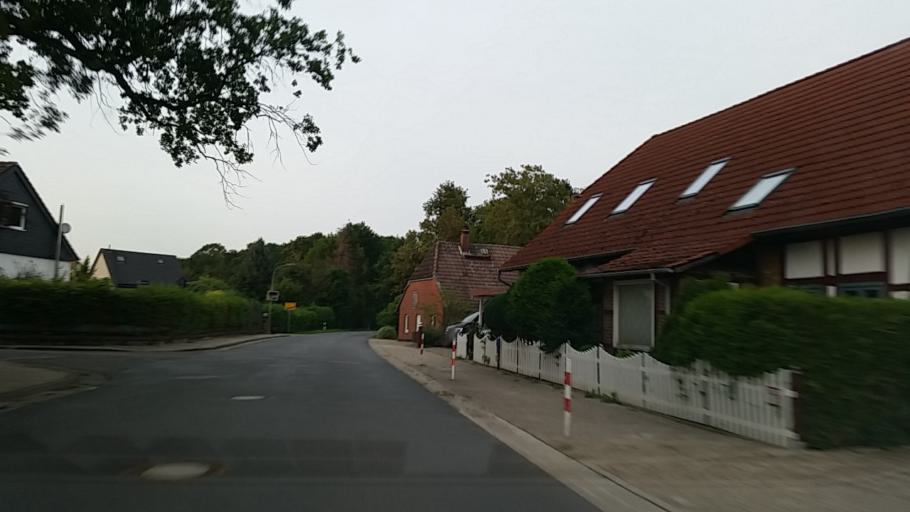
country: DE
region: Lower Saxony
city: Vordorf
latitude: 52.3586
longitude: 10.4974
